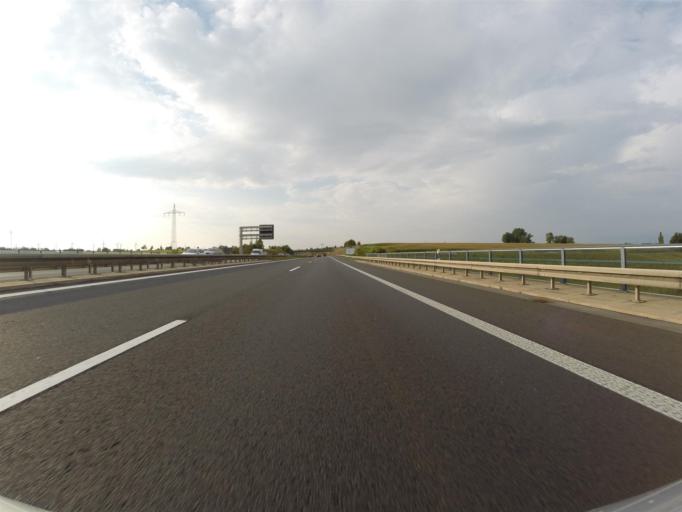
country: DE
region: Saxony-Anhalt
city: Grosskorbetha
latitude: 51.2463
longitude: 12.0229
